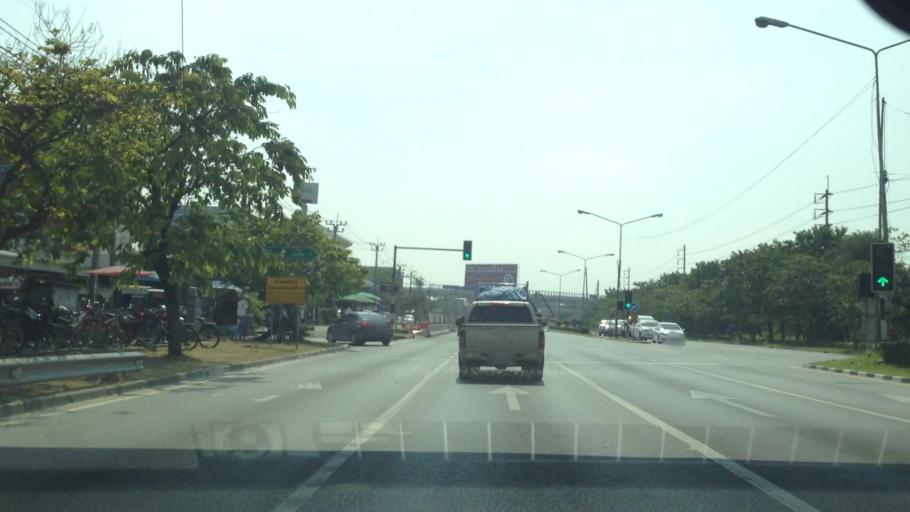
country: TH
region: Bangkok
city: Sai Mai
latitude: 13.9304
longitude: 100.6261
